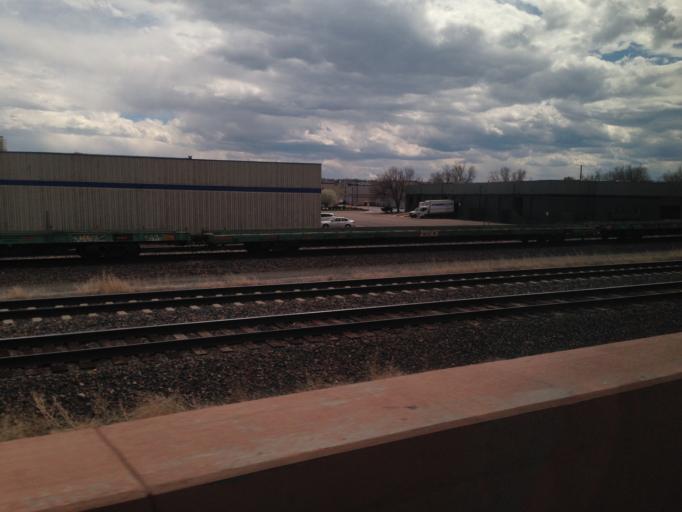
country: US
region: Colorado
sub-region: Adams County
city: Berkley
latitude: 39.8033
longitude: -105.0509
